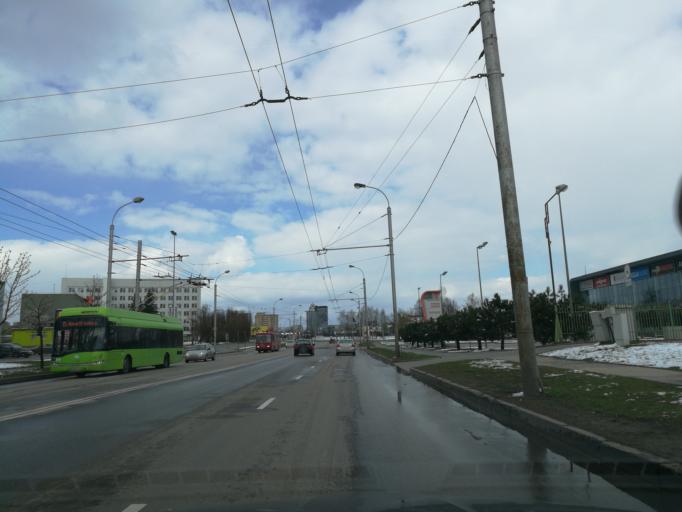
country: LT
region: Kauno apskritis
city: Dainava (Kaunas)
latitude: 54.9118
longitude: 23.9843
